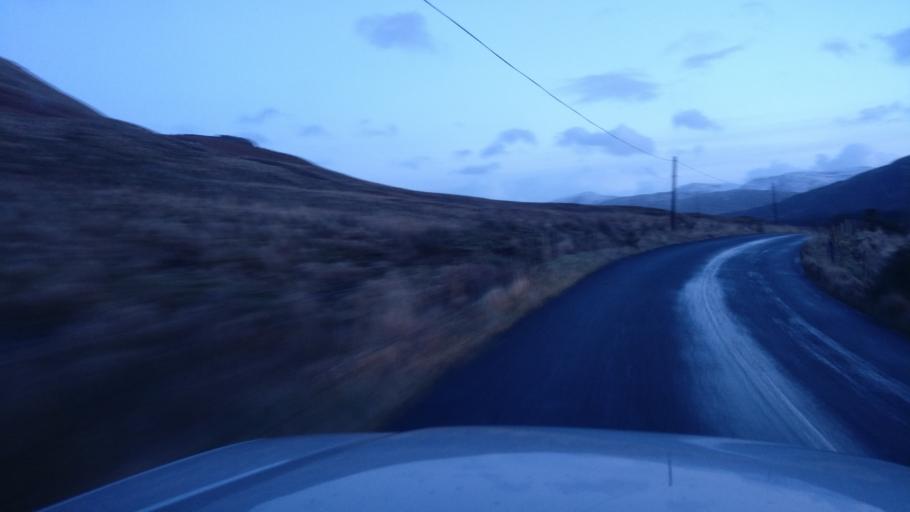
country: IE
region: Connaught
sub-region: Maigh Eo
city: Westport
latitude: 53.5632
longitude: -9.6490
